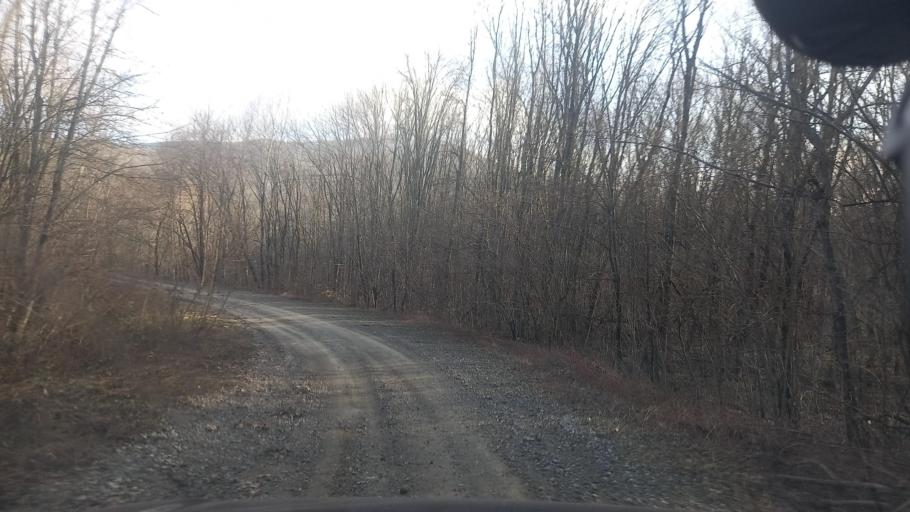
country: RU
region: Krasnodarskiy
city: Smolenskaya
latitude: 44.6794
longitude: 38.7792
